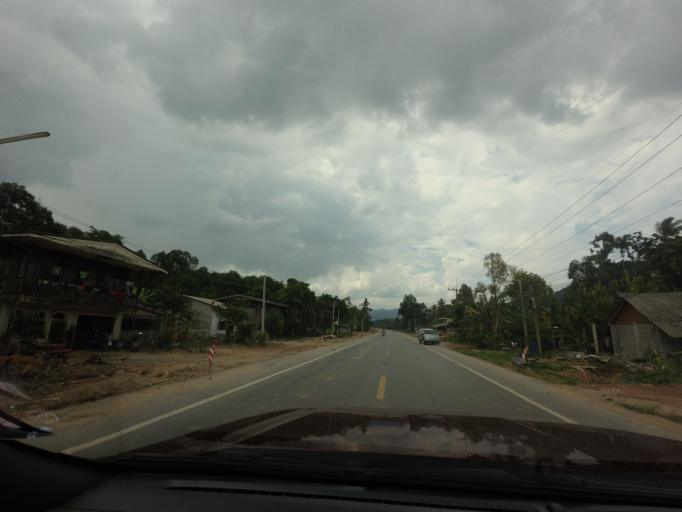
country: TH
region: Yala
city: Ban Nang Sata
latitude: 6.3075
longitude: 101.3024
